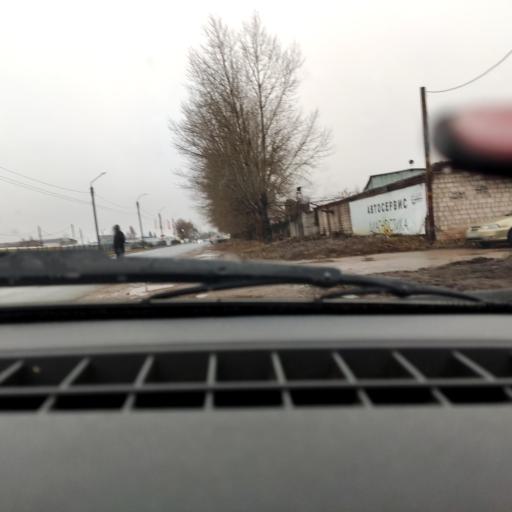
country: RU
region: Bashkortostan
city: Ufa
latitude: 54.8311
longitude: 56.0940
